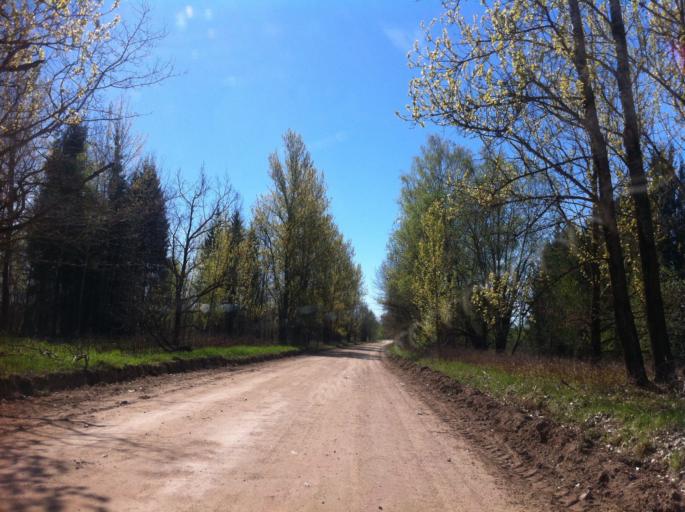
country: RU
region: Pskov
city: Izborsk
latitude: 57.7824
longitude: 27.9627
